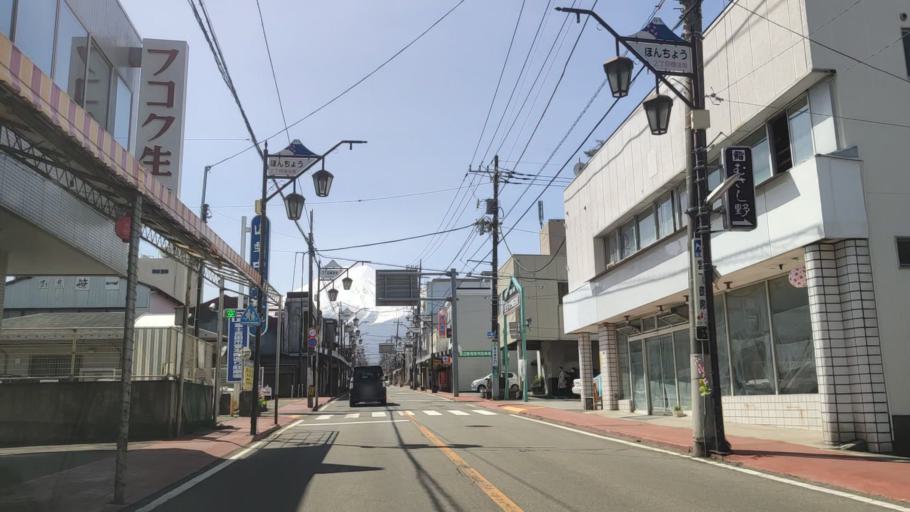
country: JP
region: Yamanashi
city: Fujikawaguchiko
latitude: 35.4925
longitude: 138.8038
